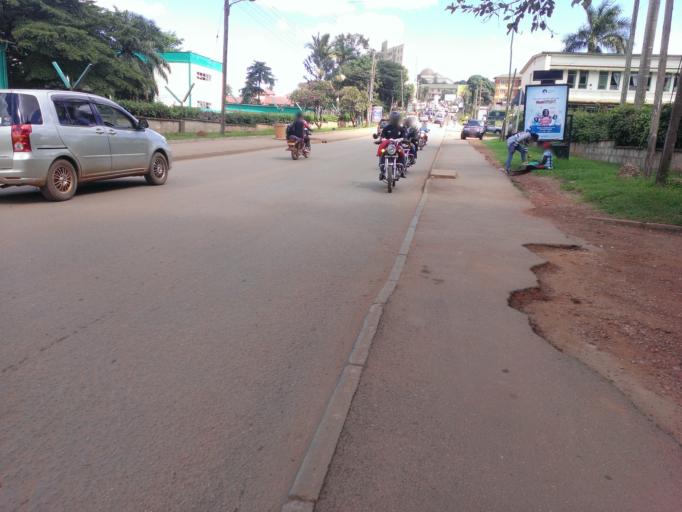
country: UG
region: Central Region
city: Kampala Central Division
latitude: 0.3211
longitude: 32.5693
